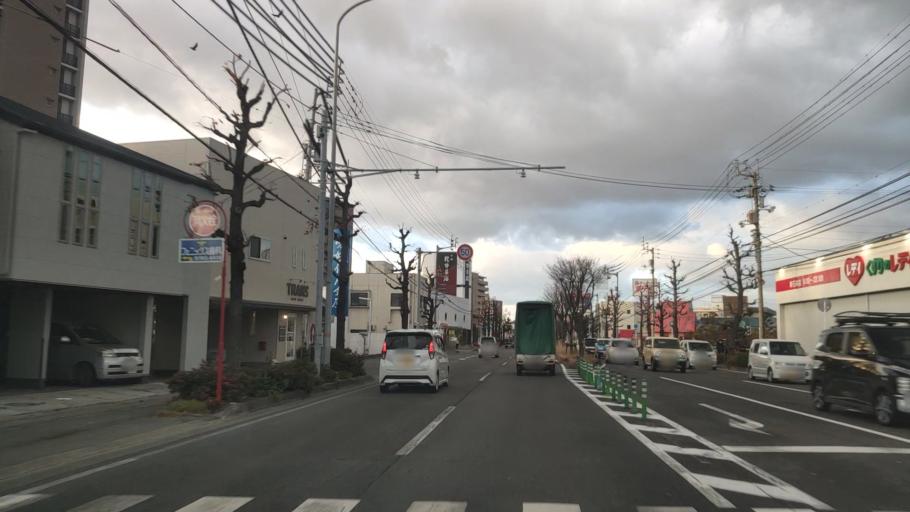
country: JP
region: Ehime
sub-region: Shikoku-chuo Shi
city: Matsuyama
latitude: 33.8139
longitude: 132.7780
